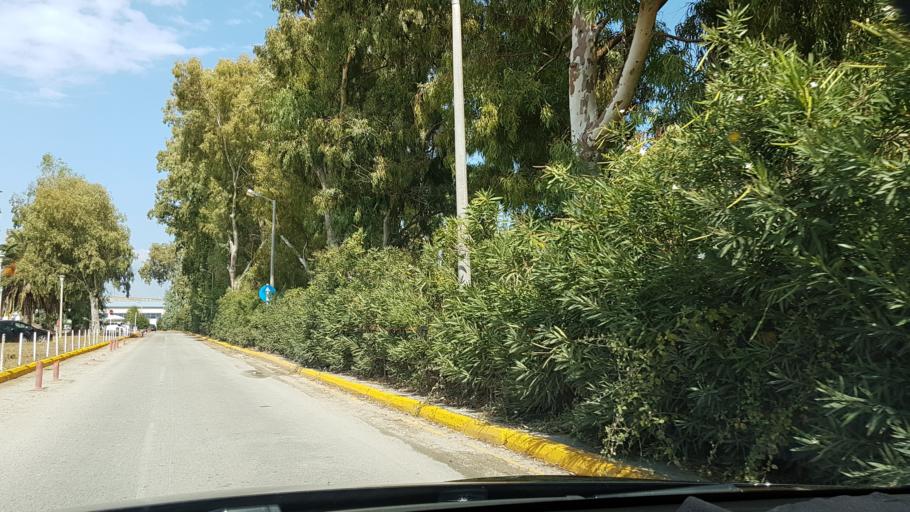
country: GR
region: Ionian Islands
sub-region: Nomos Kerkyras
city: Kerkyra
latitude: 39.6075
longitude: 19.9155
